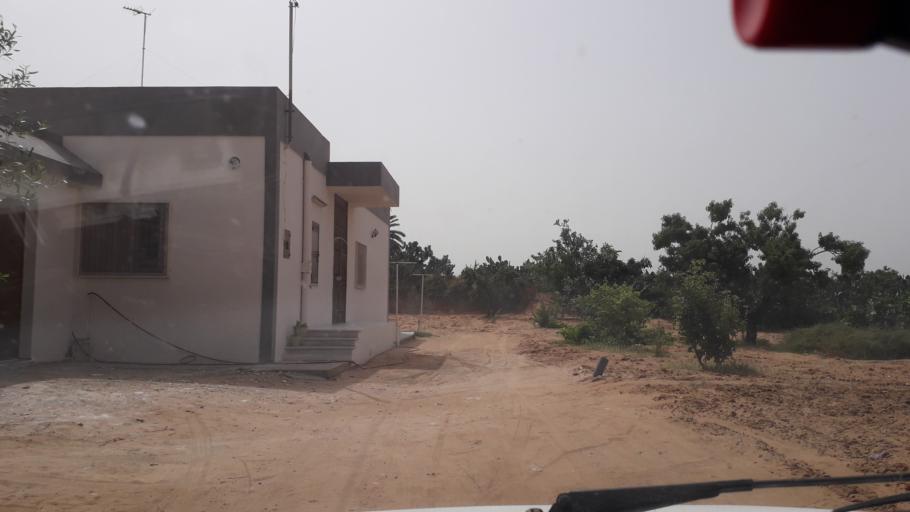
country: TN
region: Safaqis
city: Al Qarmadah
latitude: 34.8059
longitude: 10.7724
